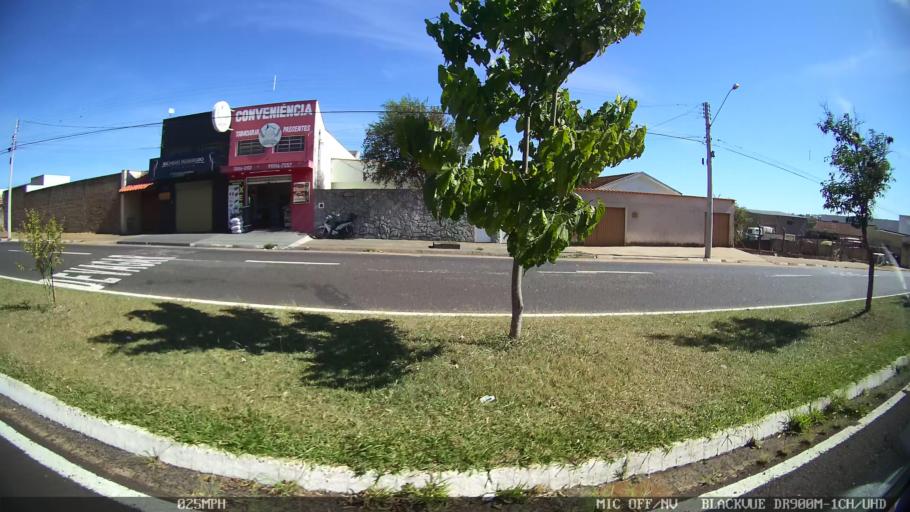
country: BR
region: Sao Paulo
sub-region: Franca
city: Franca
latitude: -20.5561
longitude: -47.3718
